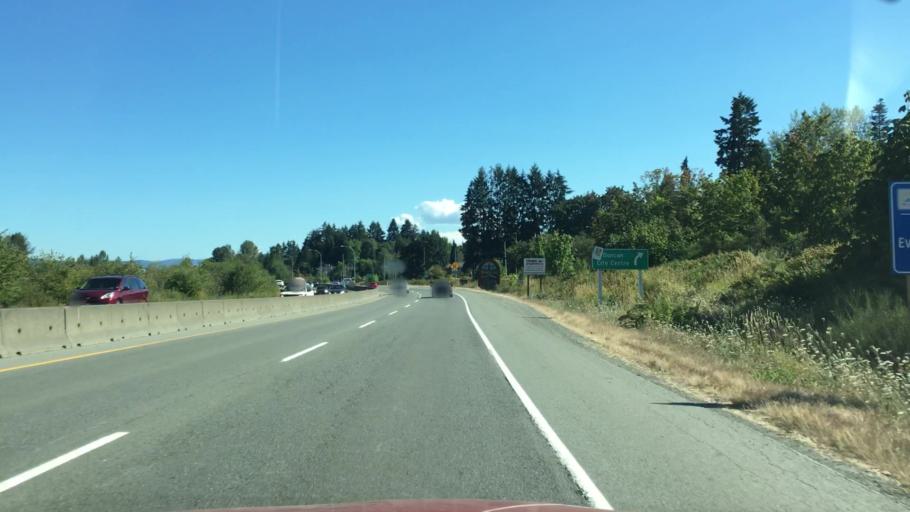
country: CA
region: British Columbia
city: Duncan
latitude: 48.7946
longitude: -123.7139
